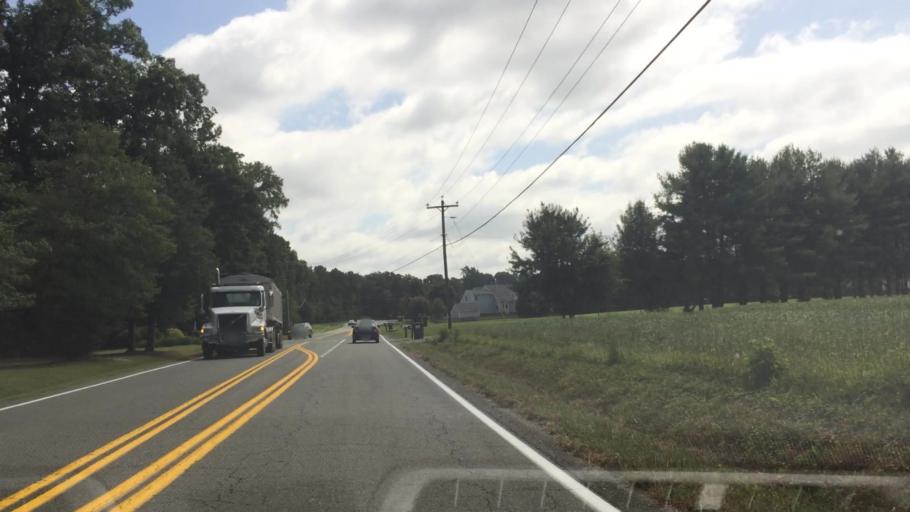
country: US
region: Virginia
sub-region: Henrico County
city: Chamberlayne
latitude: 37.6855
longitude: -77.4343
